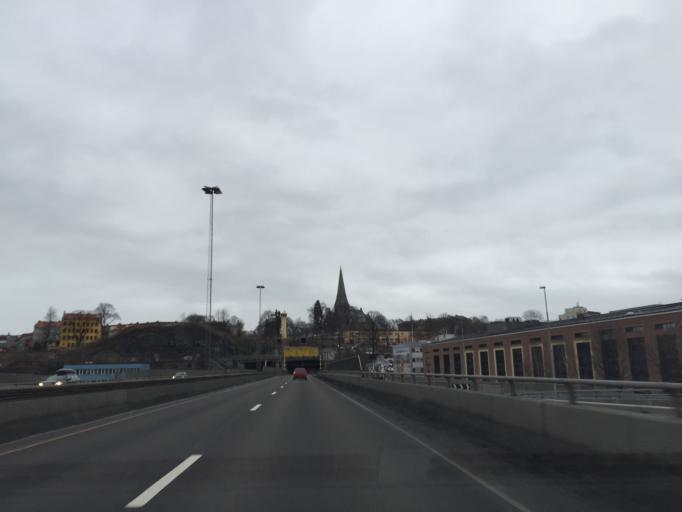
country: NO
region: Oslo
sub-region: Oslo
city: Oslo
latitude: 59.9033
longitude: 10.7834
